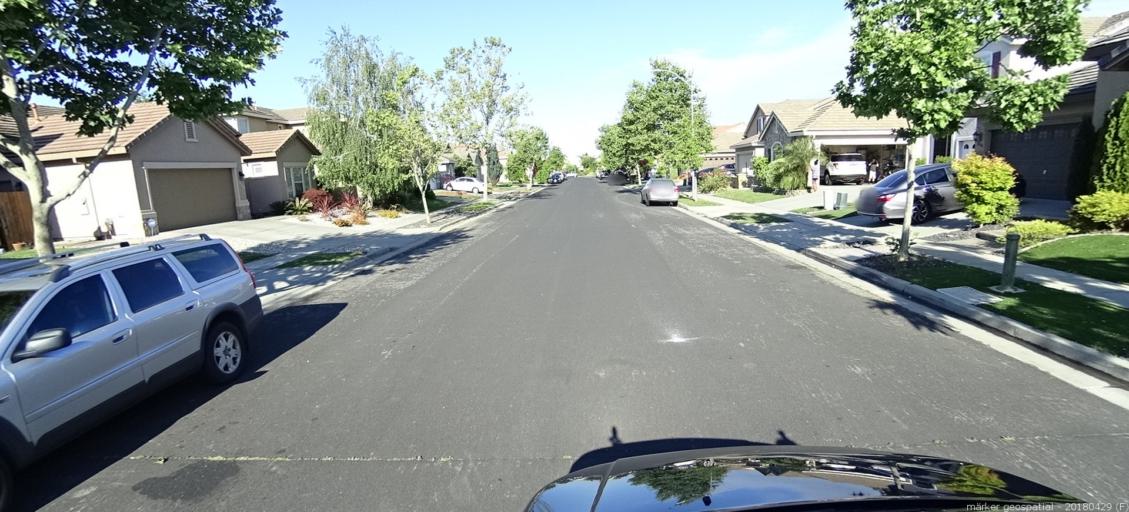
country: US
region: California
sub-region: Yolo County
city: West Sacramento
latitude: 38.5407
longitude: -121.5734
